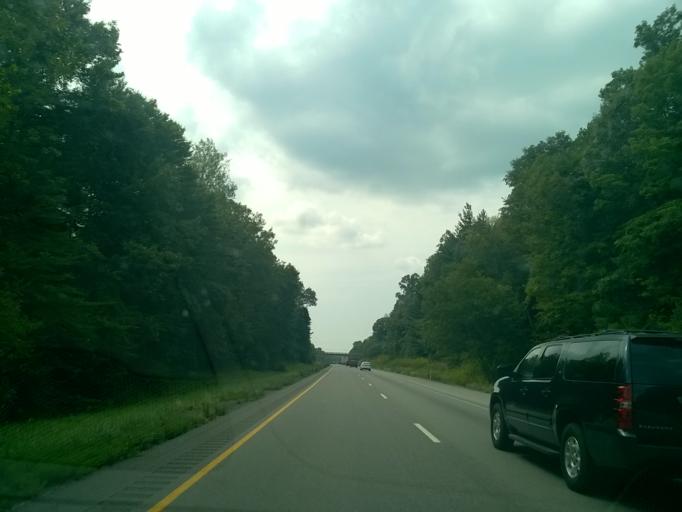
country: US
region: Indiana
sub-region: Putnam County
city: Cloverdale
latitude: 39.5192
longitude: -86.9045
